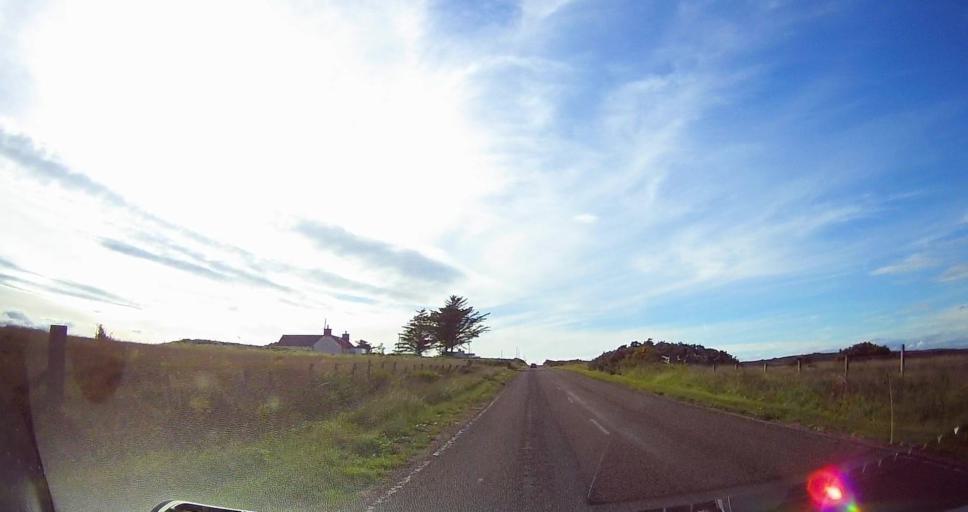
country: GB
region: Scotland
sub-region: Highland
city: Wick
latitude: 58.6424
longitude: -3.1795
